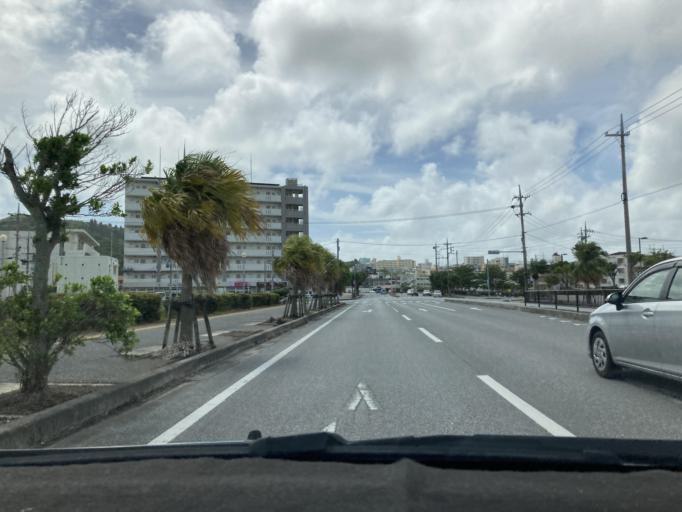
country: JP
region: Okinawa
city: Ginowan
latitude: 26.2044
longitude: 127.7615
